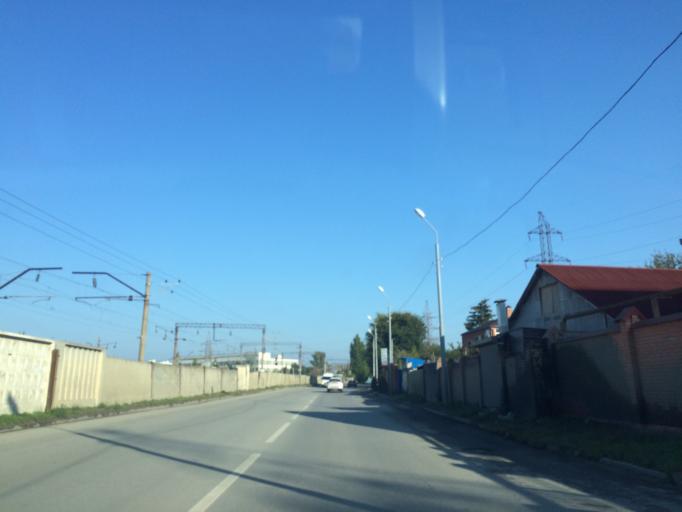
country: RU
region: Rostov
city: Rostov-na-Donu
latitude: 47.2389
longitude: 39.6718
